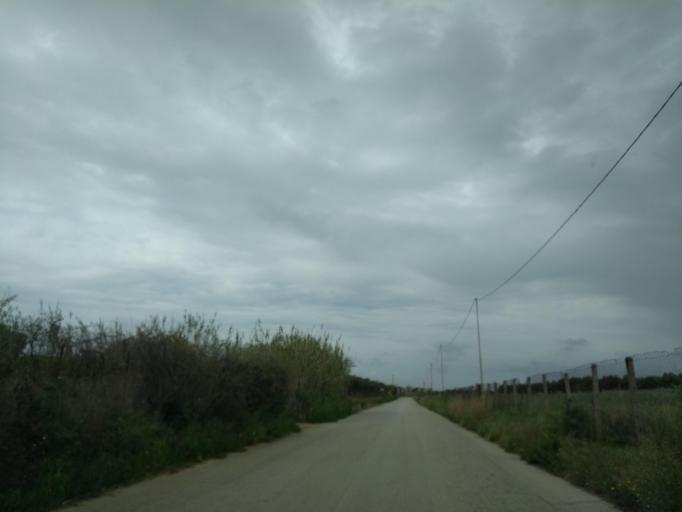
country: IT
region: Sicily
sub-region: Palermo
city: Partinico
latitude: 37.9962
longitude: 13.0656
